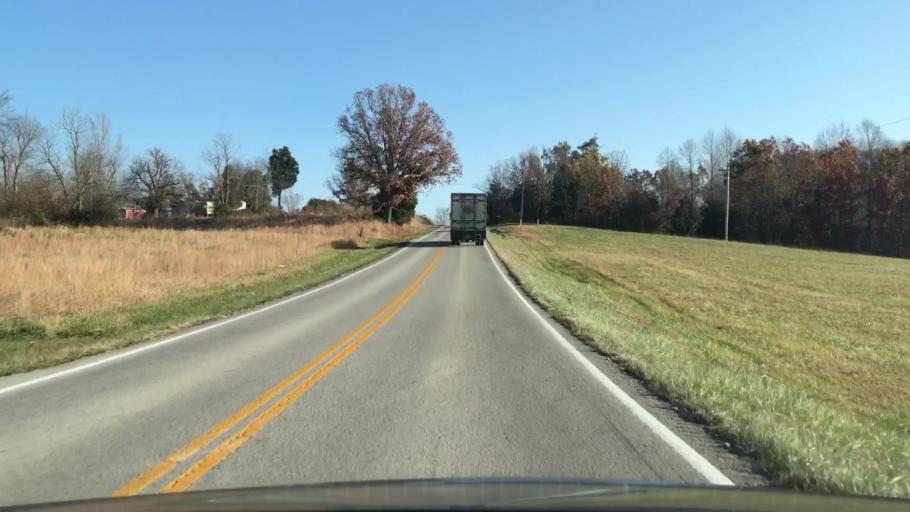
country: US
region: Kentucky
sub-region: Grayson County
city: Leitchfield
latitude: 37.3867
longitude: -86.2498
